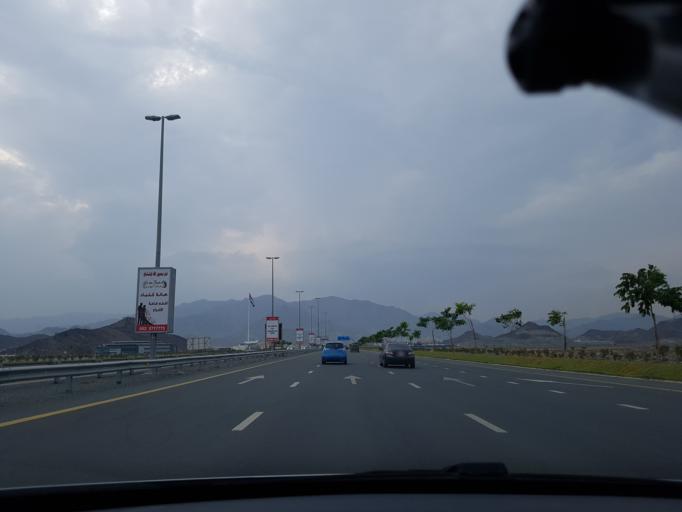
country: AE
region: Al Fujayrah
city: Al Fujayrah
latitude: 25.1227
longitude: 56.2941
